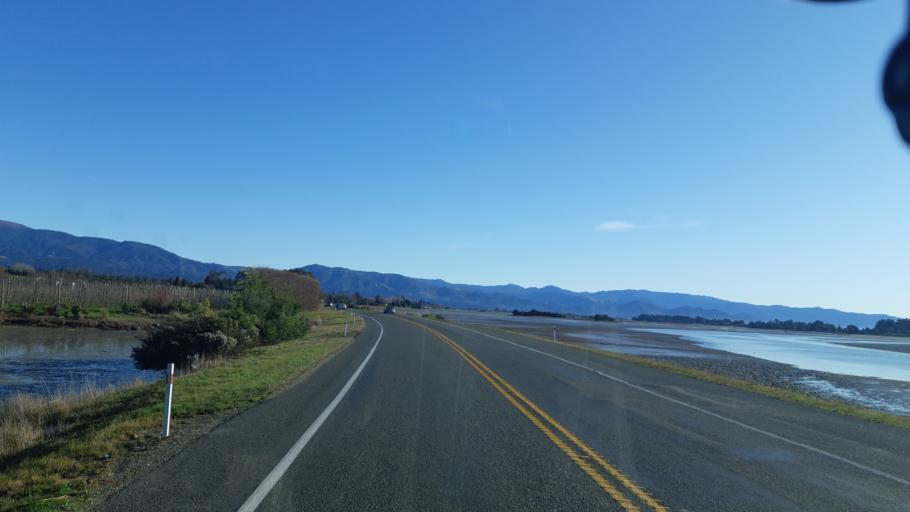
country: NZ
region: Tasman
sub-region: Tasman District
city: Motueka
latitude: -41.1766
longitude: 173.0410
